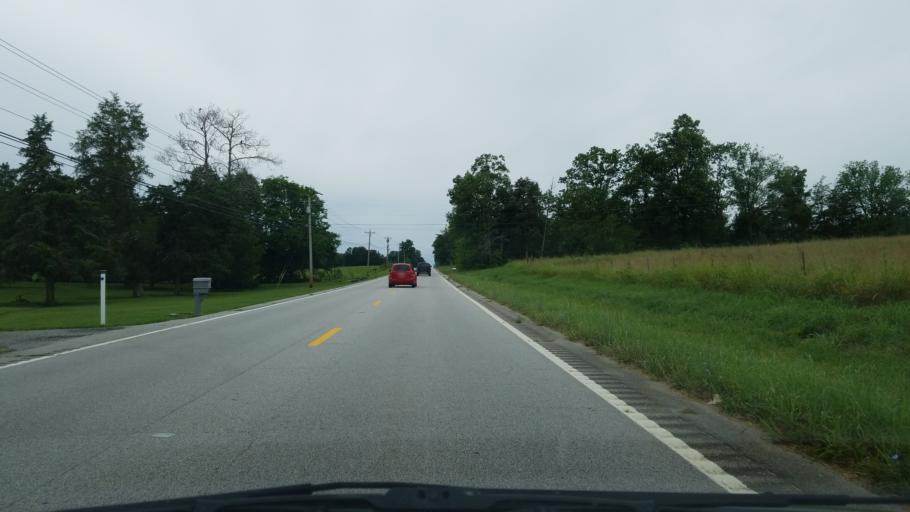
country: US
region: Tennessee
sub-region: Bradley County
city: Hopewell
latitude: 35.2897
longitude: -84.9690
